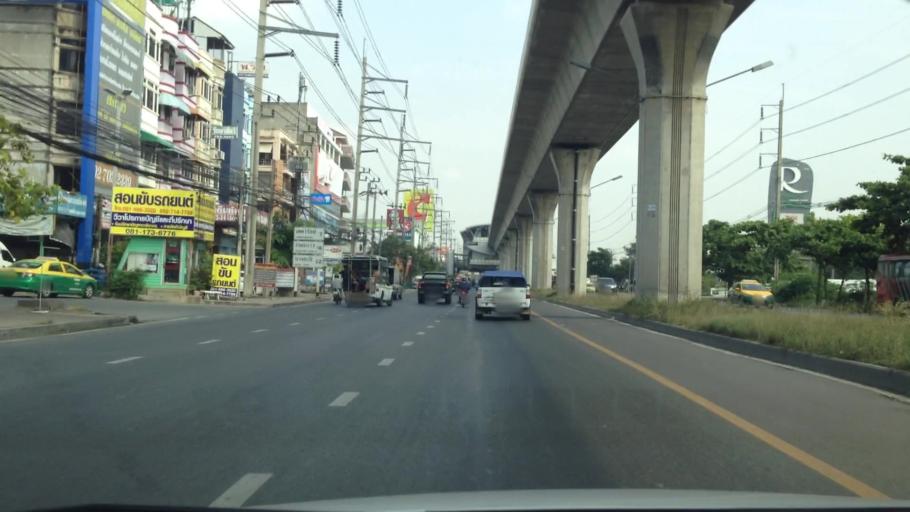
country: TH
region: Samut Prakan
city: Samut Prakan
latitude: 13.5811
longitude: 100.6066
